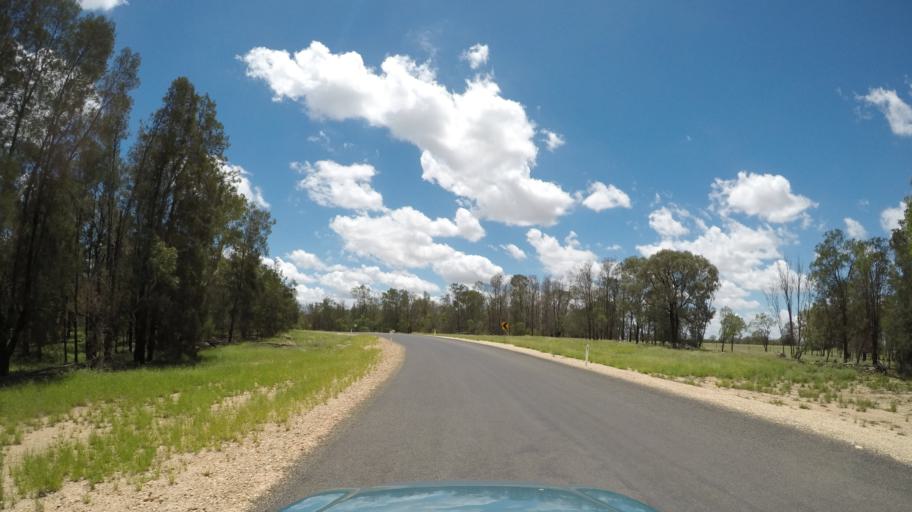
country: AU
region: Queensland
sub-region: Goondiwindi
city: Goondiwindi
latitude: -28.1497
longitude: 150.1276
